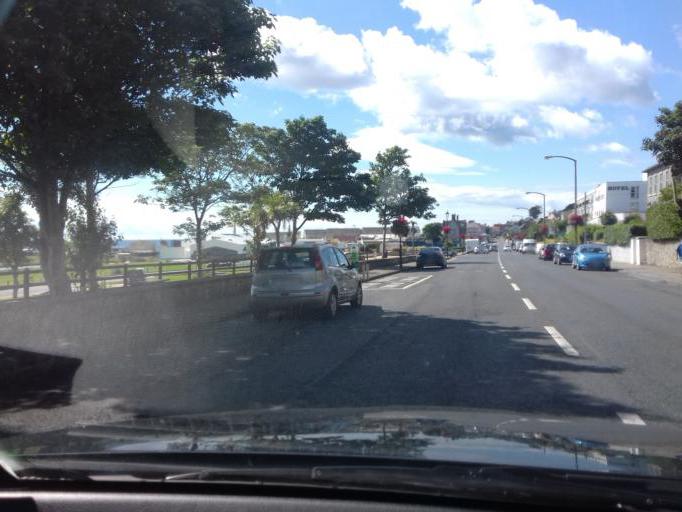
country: IE
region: Munster
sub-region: Waterford
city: Tra Mhor
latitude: 52.1642
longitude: -7.1469
